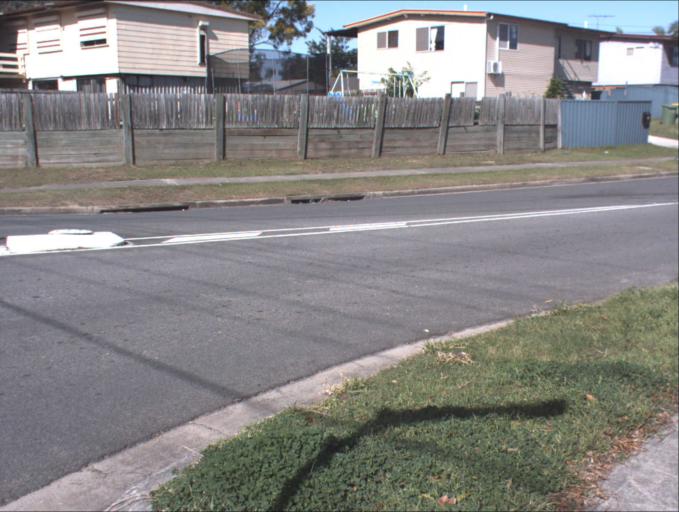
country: AU
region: Queensland
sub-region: Logan
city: Waterford West
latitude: -27.6817
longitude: 153.0929
